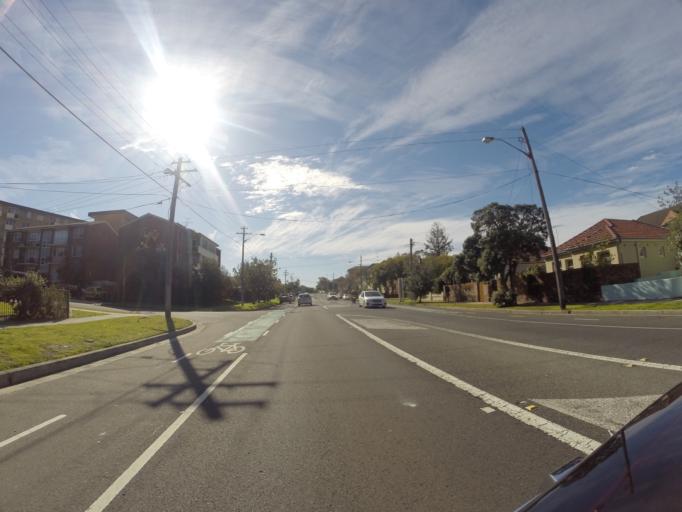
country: AU
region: New South Wales
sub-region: Randwick
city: South Coogee
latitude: -33.9363
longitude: 151.2577
